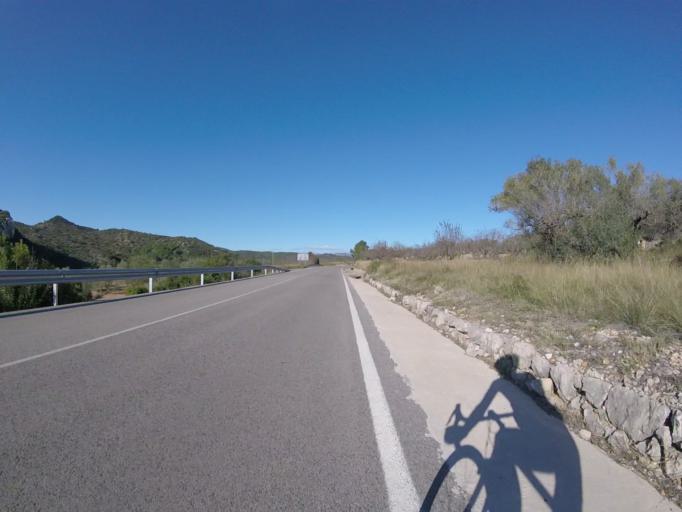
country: ES
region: Valencia
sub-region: Provincia de Castello
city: Cervera del Maestre
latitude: 40.4622
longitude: 0.2548
